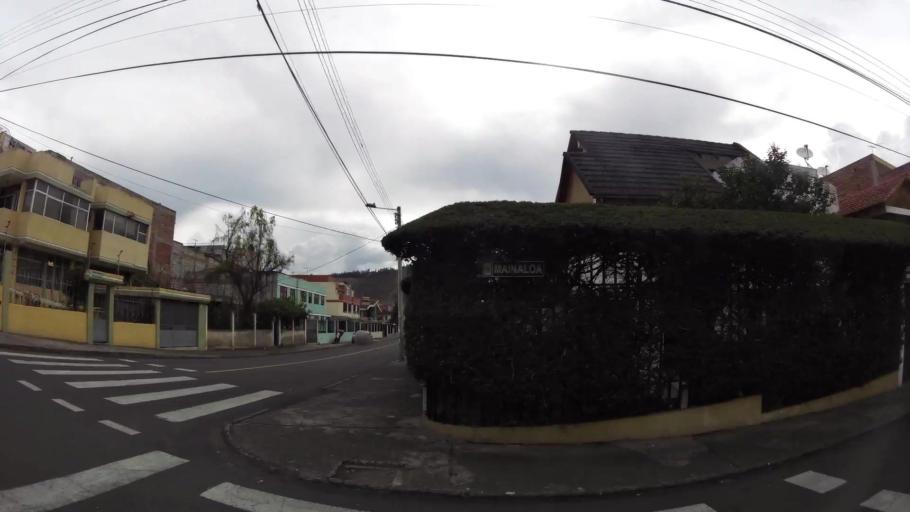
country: EC
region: Tungurahua
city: Ambato
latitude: -1.2513
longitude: -78.6297
